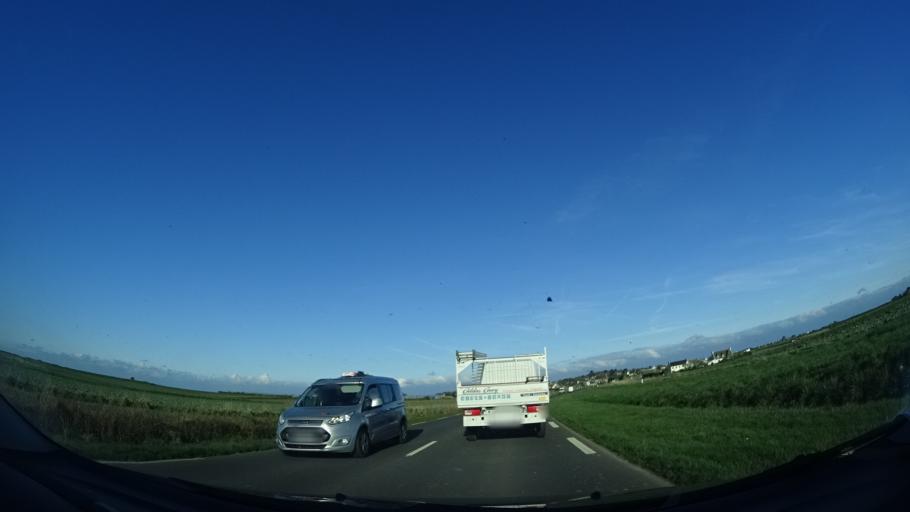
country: FR
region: Brittany
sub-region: Departement du Finistere
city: Saint-Pol-de-Leon
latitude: 48.6927
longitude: -3.9985
